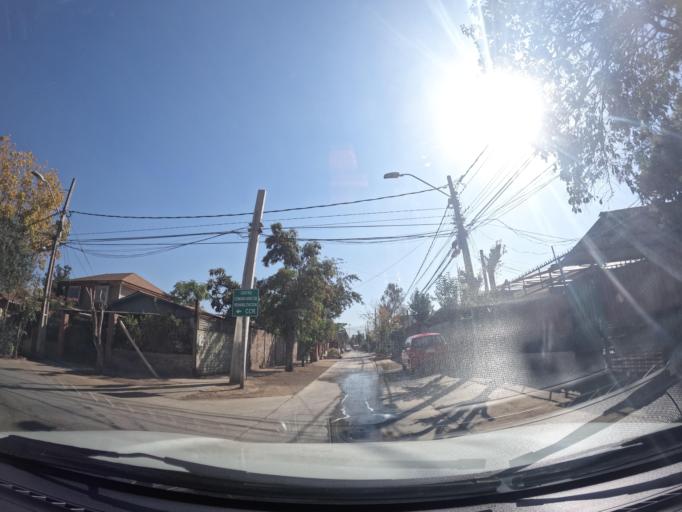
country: CL
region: Santiago Metropolitan
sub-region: Provincia de Santiago
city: Villa Presidente Frei, Nunoa, Santiago, Chile
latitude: -33.4645
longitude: -70.5634
